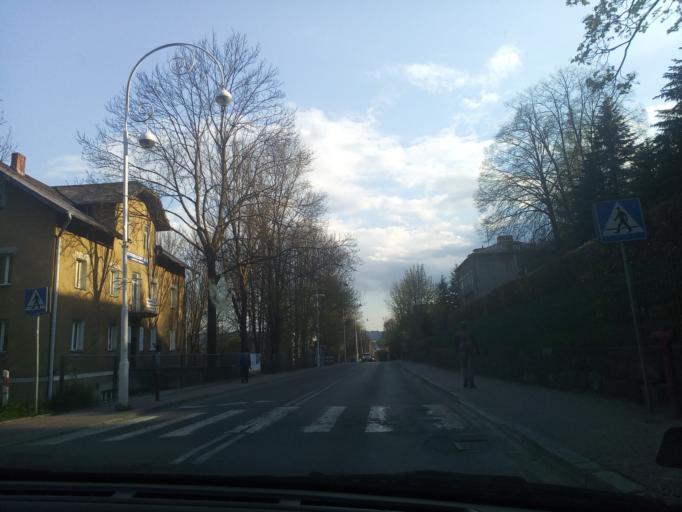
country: PL
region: Lesser Poland Voivodeship
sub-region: Powiat nowosadecki
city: Krynica-Zdroj
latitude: 49.4099
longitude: 20.9547
